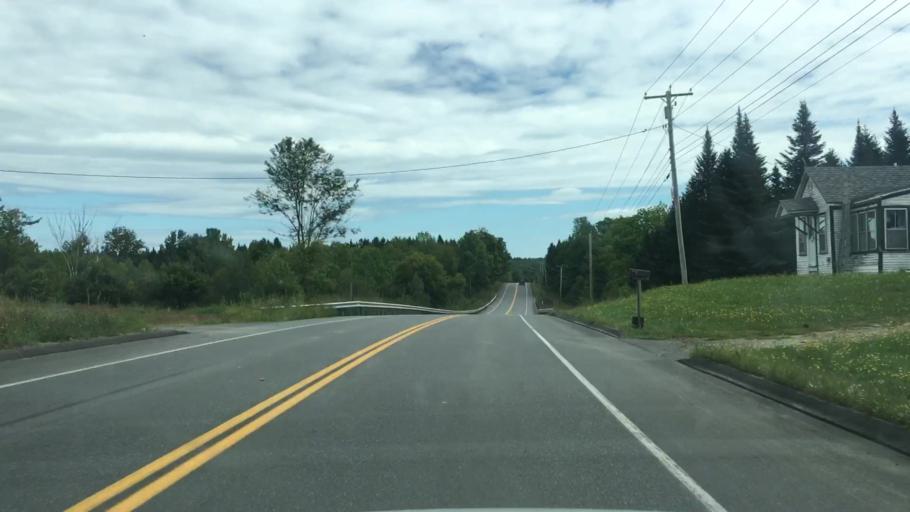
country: US
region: Maine
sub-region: Piscataquis County
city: Milo
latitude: 45.2404
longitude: -69.0444
